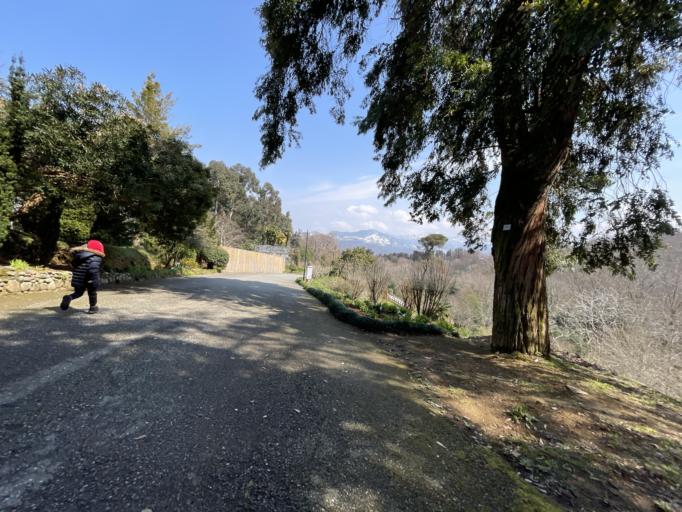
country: GE
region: Ajaria
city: Makhinjauri
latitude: 41.6994
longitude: 41.7175
